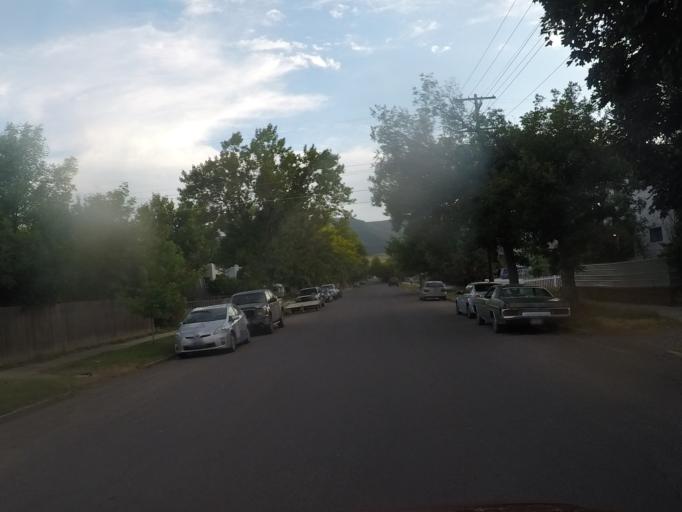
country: US
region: Montana
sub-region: Park County
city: Livingston
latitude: 45.6558
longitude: -110.5615
